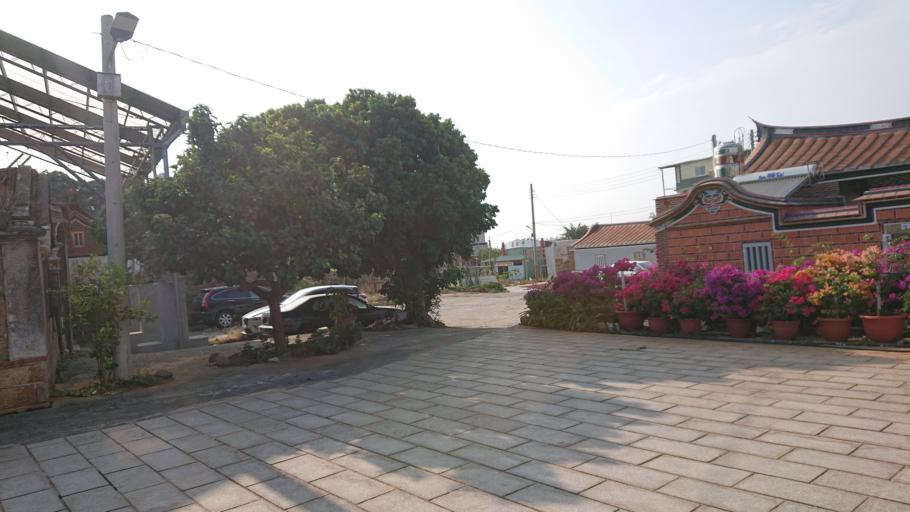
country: TW
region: Fukien
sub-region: Kinmen
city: Jincheng
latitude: 24.4791
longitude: 118.4282
